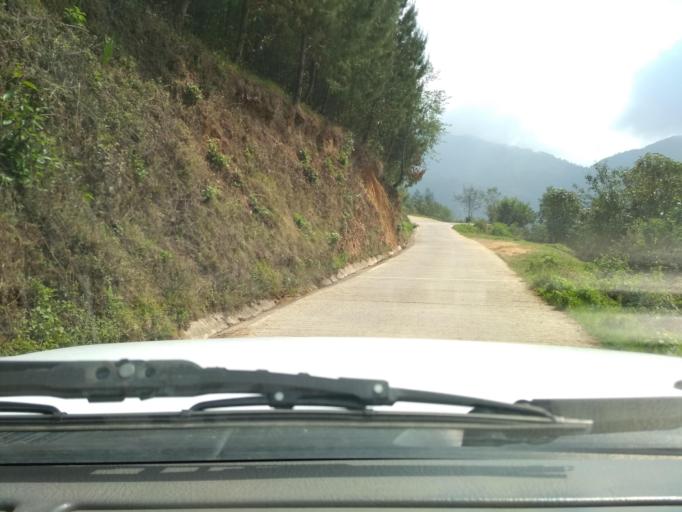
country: MX
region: Veracruz
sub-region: Camerino Z. Mendoza
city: Necoxtla
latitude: 18.7723
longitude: -97.1552
